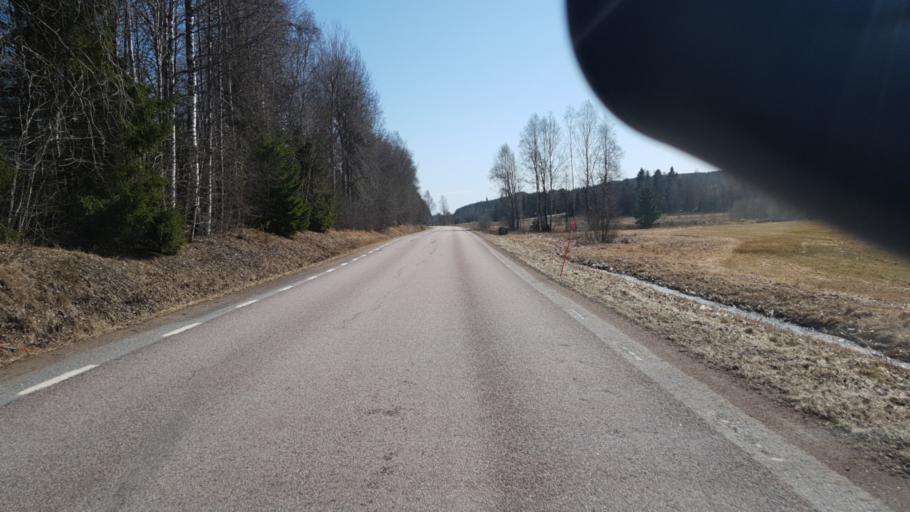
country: SE
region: Vaermland
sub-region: Arvika Kommun
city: Arvika
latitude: 59.6725
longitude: 12.7970
